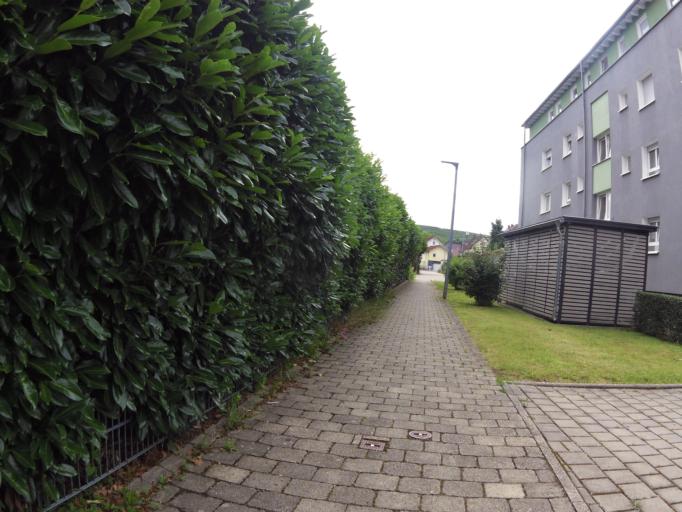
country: DE
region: Baden-Wuerttemberg
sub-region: Freiburg Region
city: Lahr
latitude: 48.3488
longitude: 7.8347
